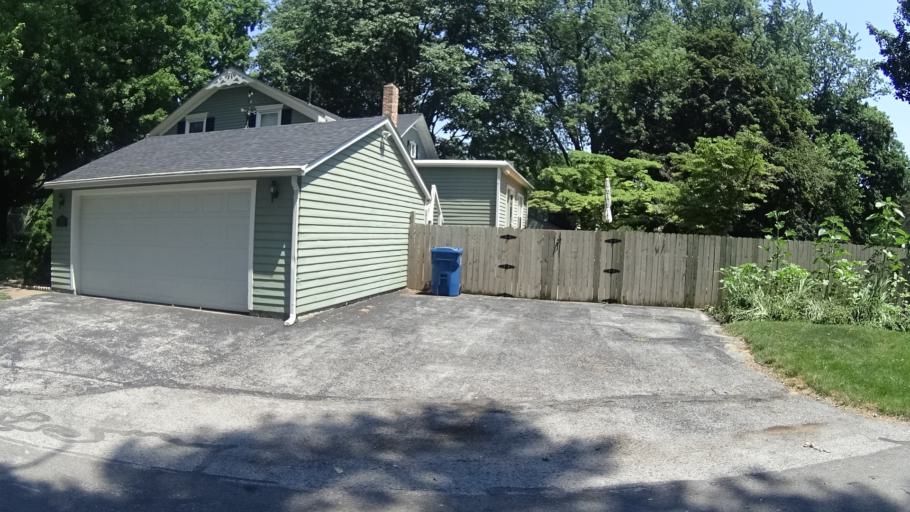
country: US
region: Ohio
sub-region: Erie County
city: Sandusky
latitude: 41.4098
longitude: -82.6450
